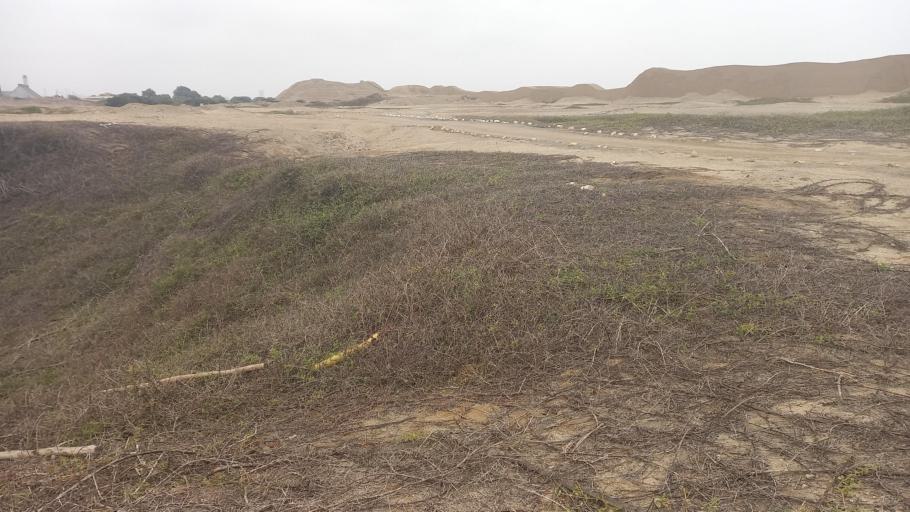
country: PE
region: La Libertad
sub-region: Provincia de Trujillo
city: La Esperanza
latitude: -8.1006
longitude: -79.0709
